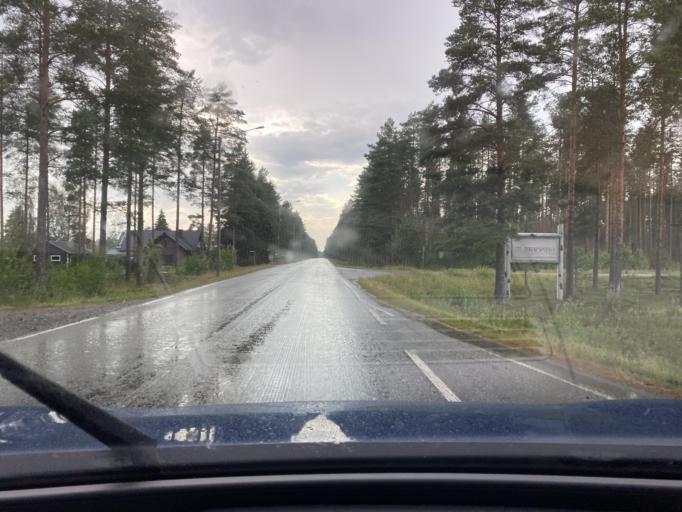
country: FI
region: Central Ostrobothnia
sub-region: Kaustinen
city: Veteli
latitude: 63.4690
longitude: 23.8232
